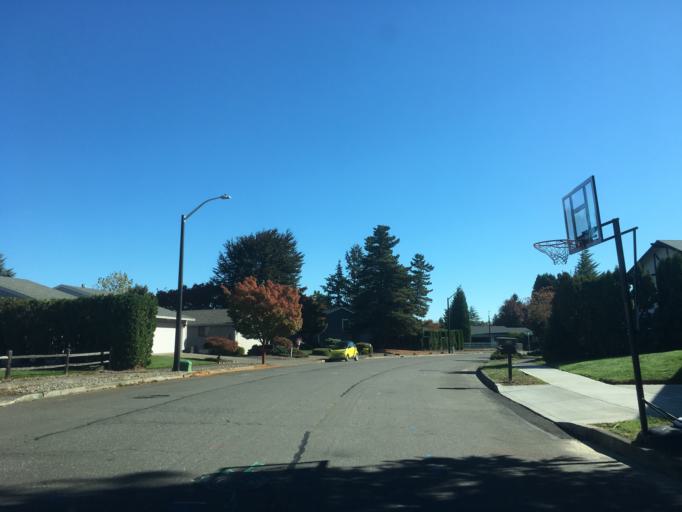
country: US
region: Oregon
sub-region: Multnomah County
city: Gresham
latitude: 45.4846
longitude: -122.4029
